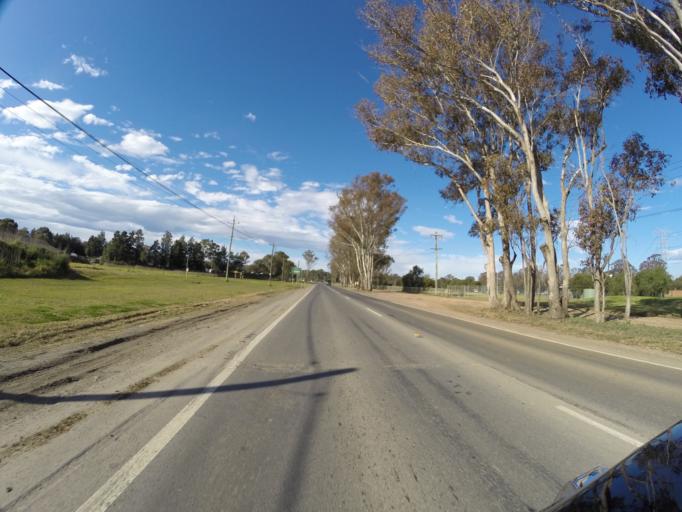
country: AU
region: New South Wales
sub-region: Fairfield
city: Cecil Park
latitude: -33.8808
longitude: 150.8050
